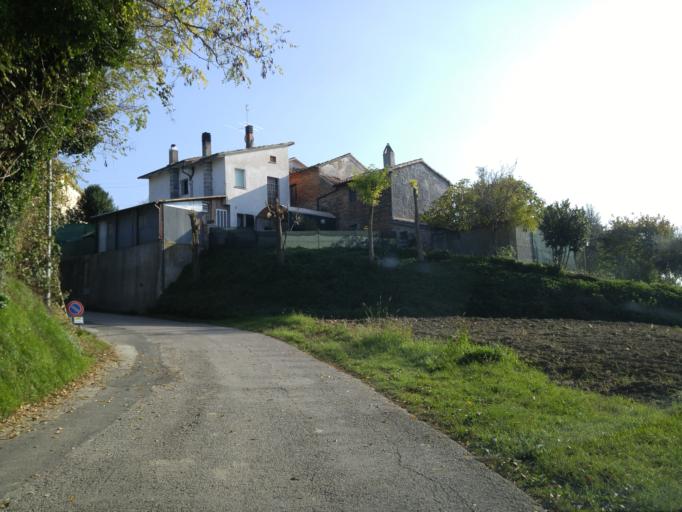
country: IT
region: The Marches
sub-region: Provincia di Pesaro e Urbino
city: Montemaggiore al Metauro
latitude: 43.7357
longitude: 12.9422
